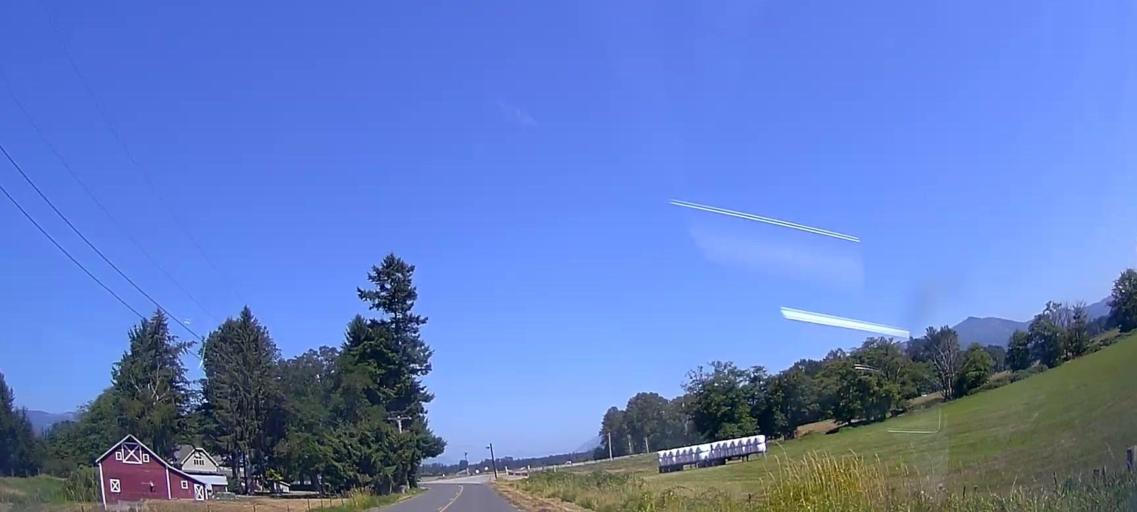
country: US
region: Washington
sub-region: Skagit County
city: Burlington
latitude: 48.4824
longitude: -122.2996
